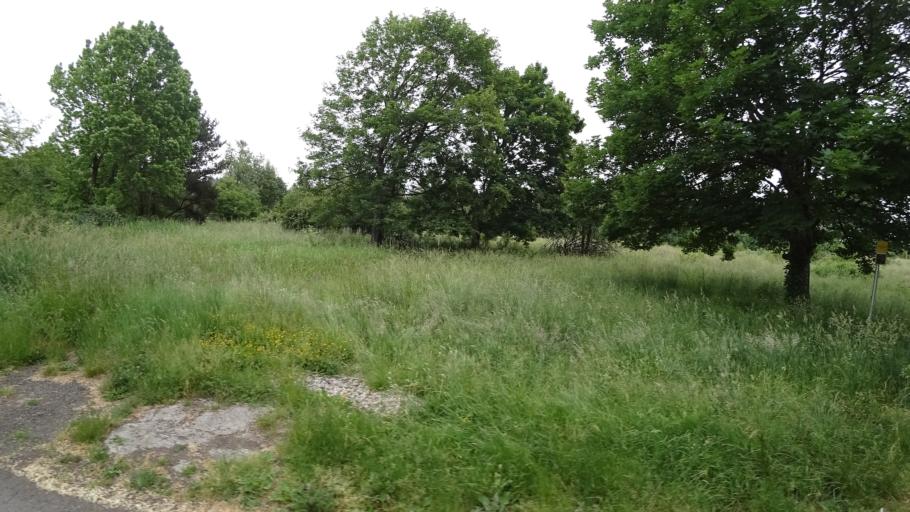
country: US
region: Oregon
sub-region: Multnomah County
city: Lents
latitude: 45.4668
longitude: -122.5744
